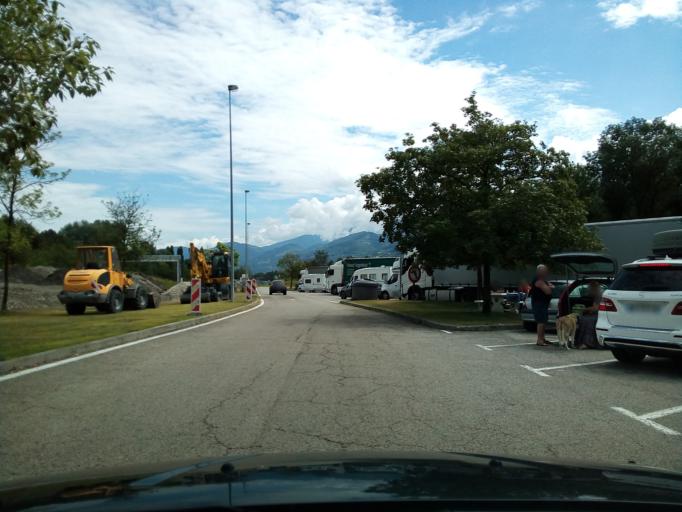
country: FR
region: Rhone-Alpes
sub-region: Departement de l'Isere
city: Saint-Nazaire-les-Eymes
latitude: 45.2439
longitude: 5.8618
